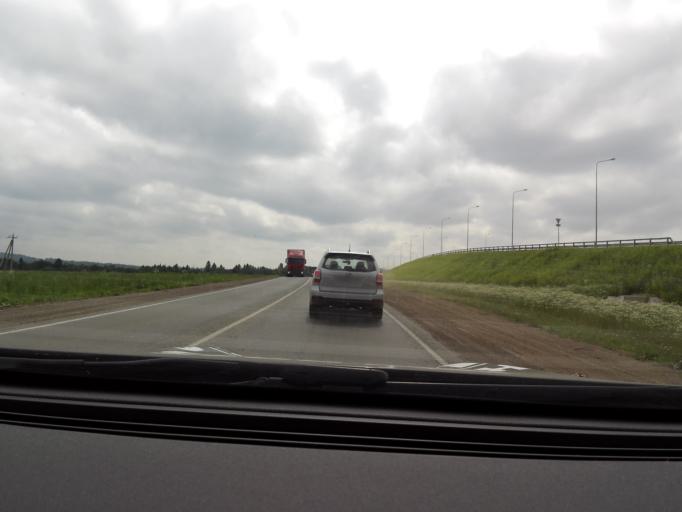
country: RU
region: Perm
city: Zvezdnyy
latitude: 57.7837
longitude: 56.3430
